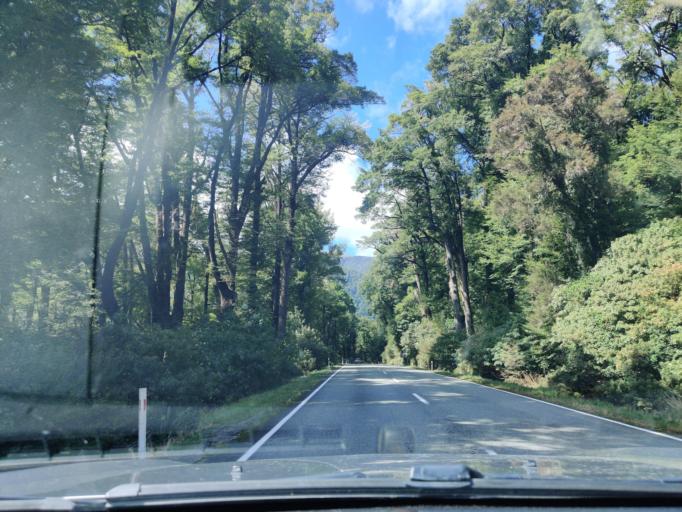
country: NZ
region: West Coast
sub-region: Buller District
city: Westport
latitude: -42.3535
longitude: 172.2354
